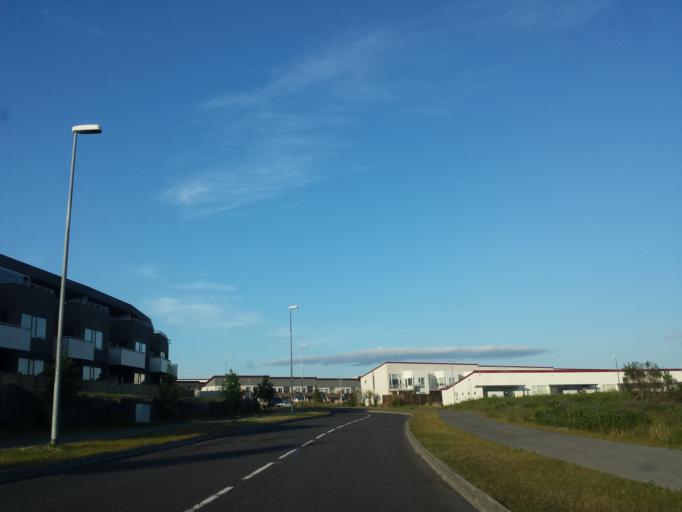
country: IS
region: Capital Region
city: Mosfellsbaer
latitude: 64.1005
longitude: -21.7683
